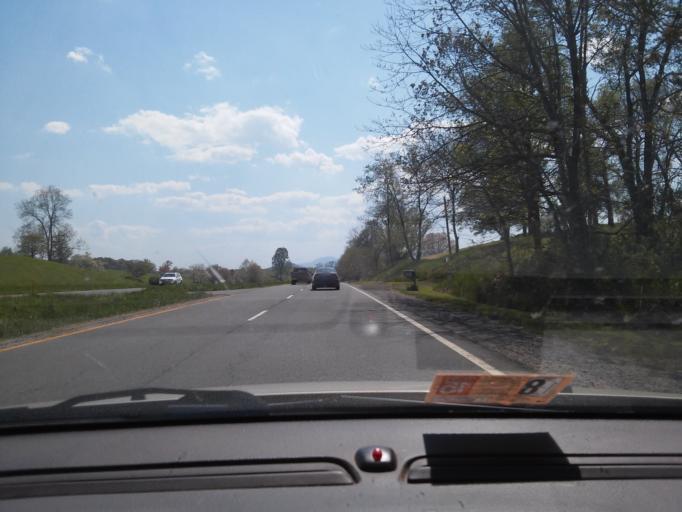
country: US
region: Virginia
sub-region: Rappahannock County
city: Washington
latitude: 38.7187
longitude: -78.1231
